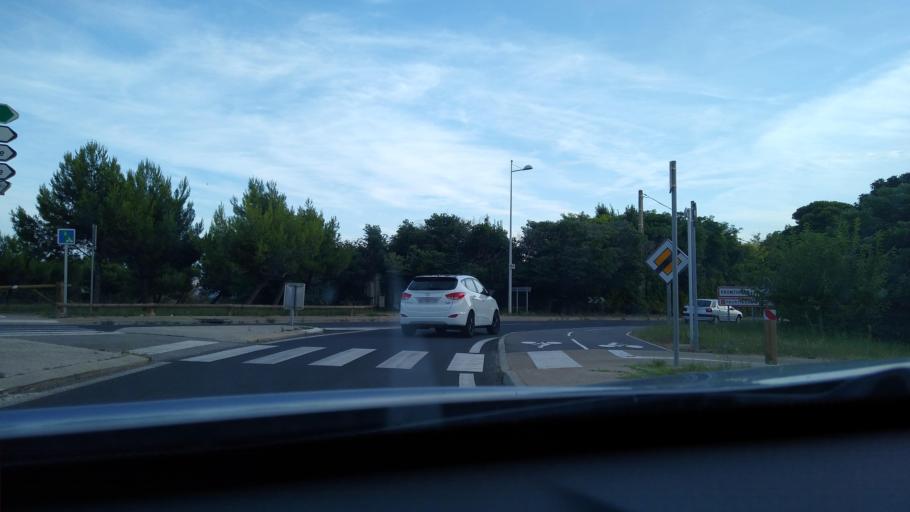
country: FR
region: Languedoc-Roussillon
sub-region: Departement de l'Herault
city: Sete
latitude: 43.4233
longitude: 3.7225
